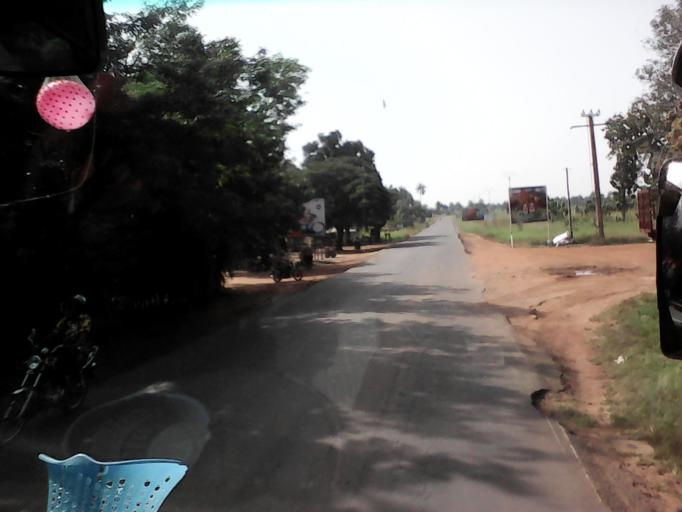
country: TG
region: Centrale
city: Sokode
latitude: 8.9654
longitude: 1.1361
